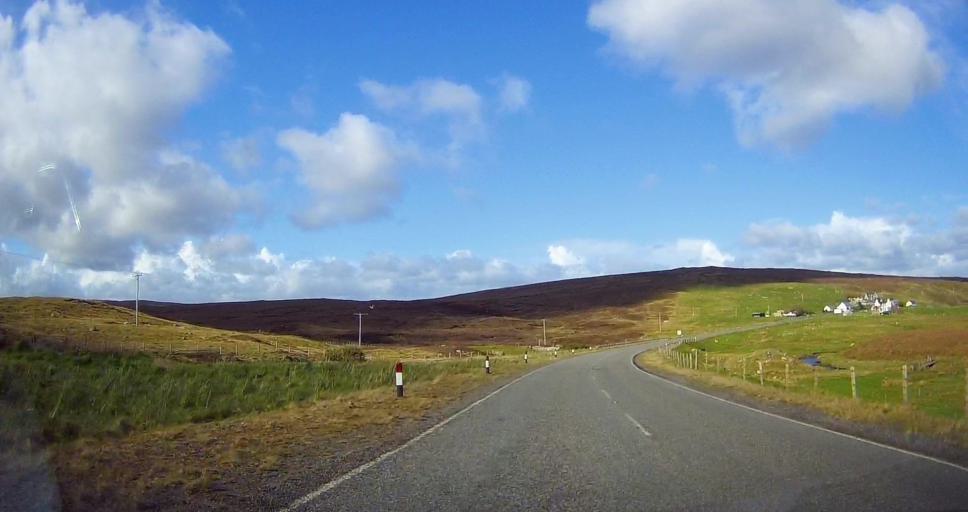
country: GB
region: Scotland
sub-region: Shetland Islands
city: Lerwick
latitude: 60.3515
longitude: -1.2055
